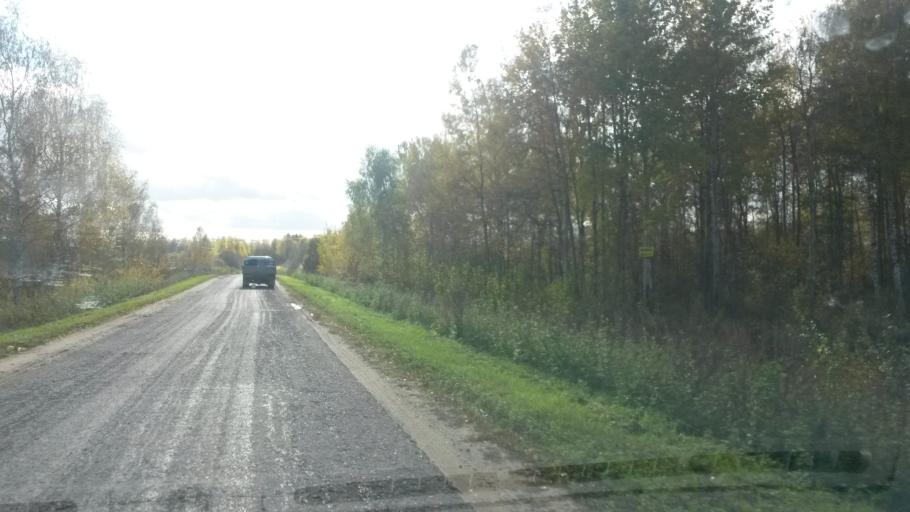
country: RU
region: Jaroslavl
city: Tunoshna
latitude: 57.5319
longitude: 40.0150
